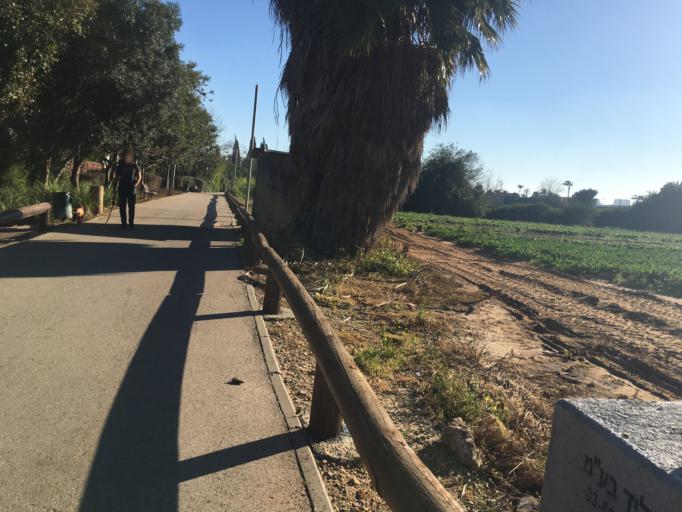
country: IL
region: Tel Aviv
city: Ramat HaSharon
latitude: 32.1440
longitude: 34.8264
